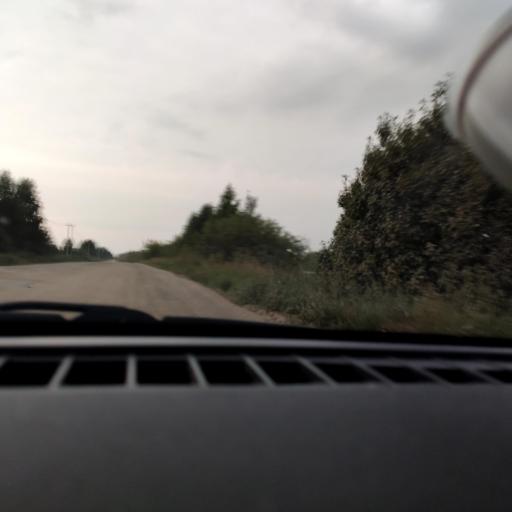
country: RU
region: Perm
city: Kondratovo
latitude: 57.9994
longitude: 56.0076
